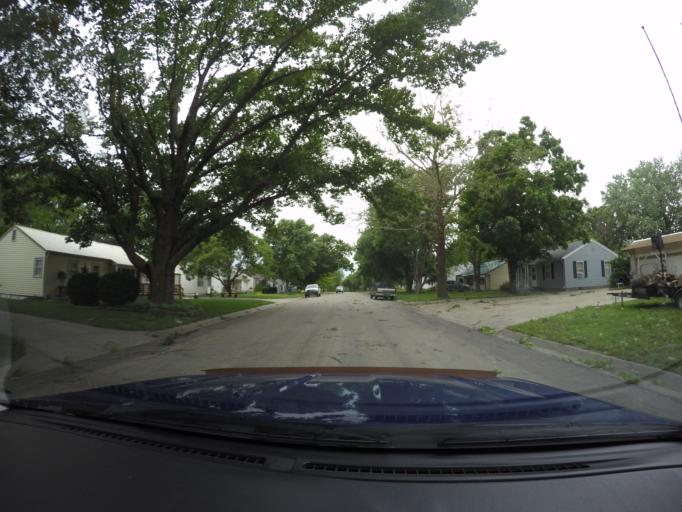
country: US
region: Kansas
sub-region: Clay County
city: Clay Center
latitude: 39.3896
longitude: -97.1230
